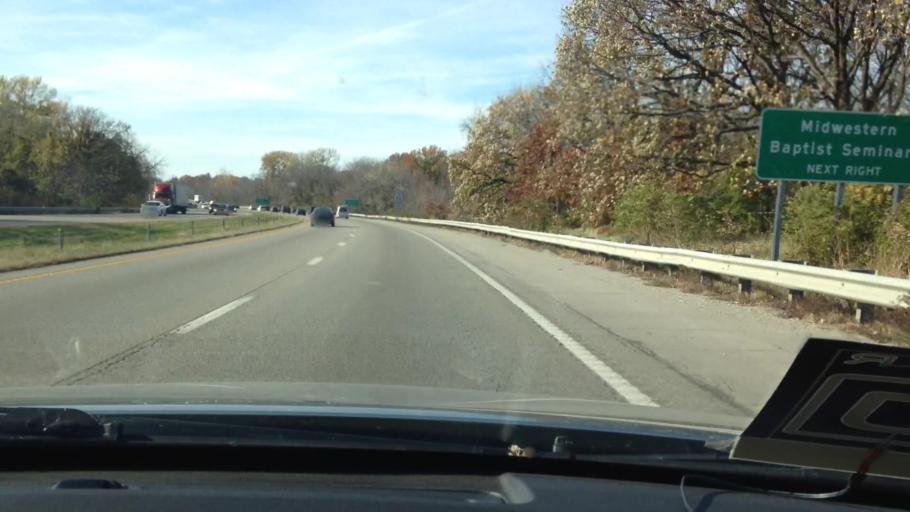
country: US
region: Missouri
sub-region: Clay County
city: Gladstone
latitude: 39.1780
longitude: -94.5646
